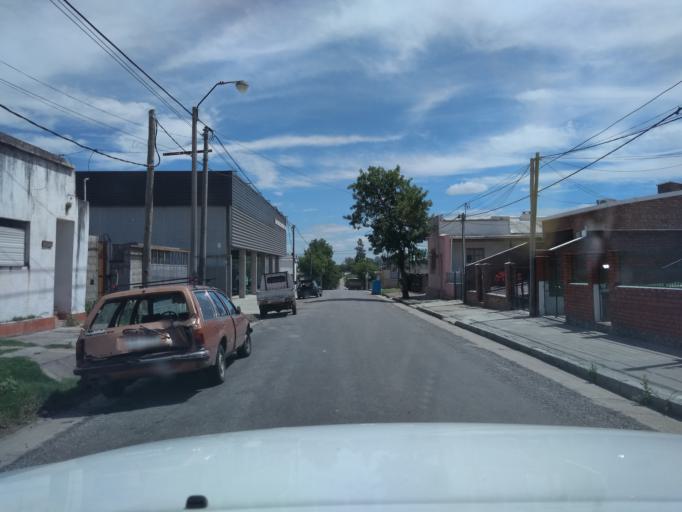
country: UY
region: Florida
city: Florida
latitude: -34.1038
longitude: -56.2172
